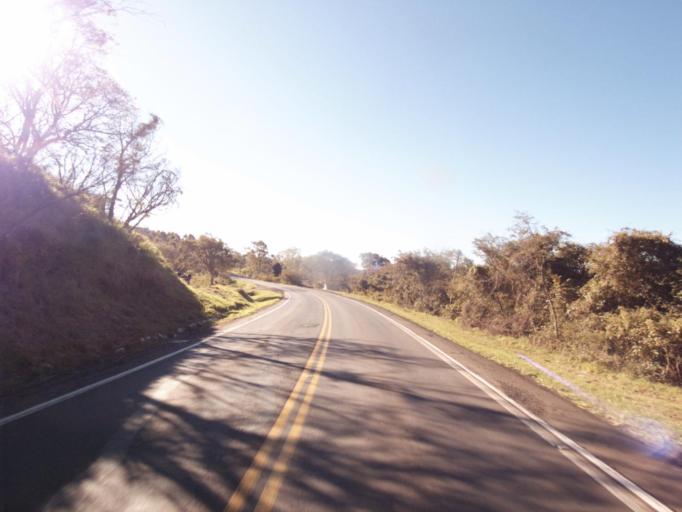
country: AR
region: Misiones
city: Bernardo de Irigoyen
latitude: -26.4941
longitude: -53.5015
